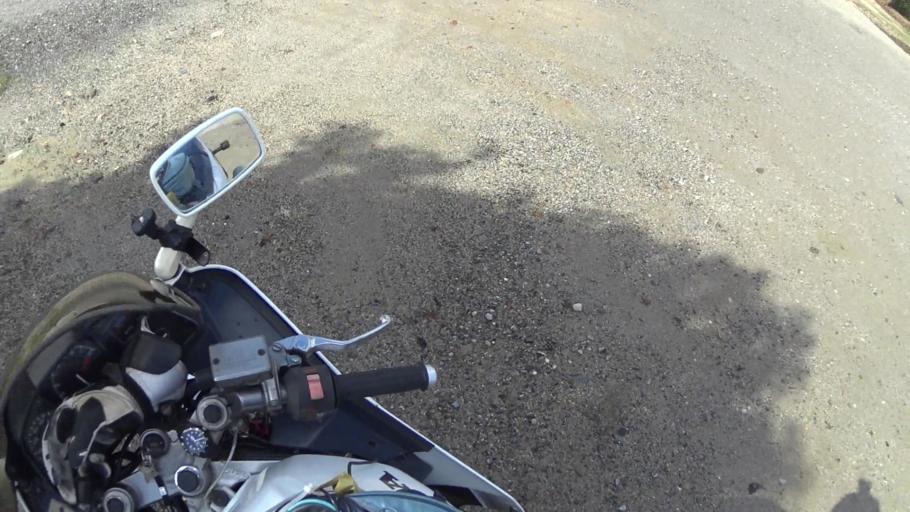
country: JP
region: Kyoto
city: Miyazu
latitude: 35.6009
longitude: 135.1865
